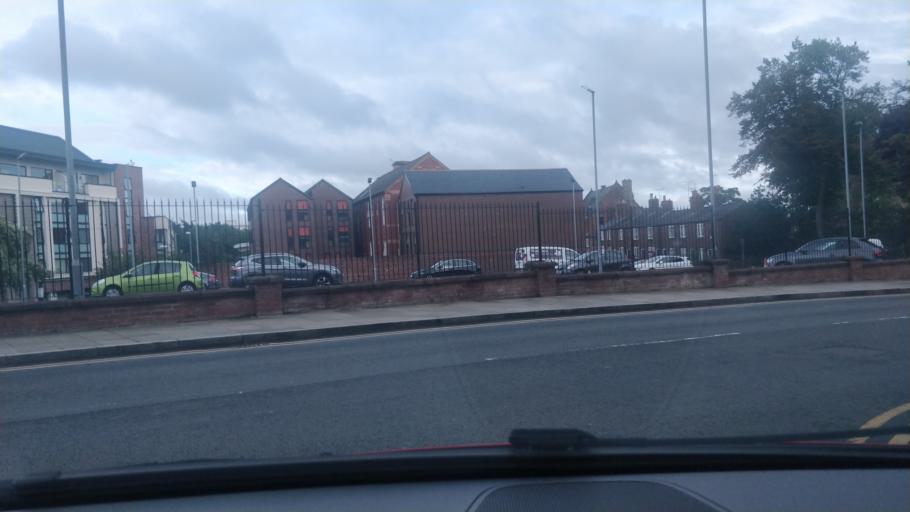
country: GB
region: England
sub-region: Cheshire West and Chester
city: Chester
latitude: 53.1949
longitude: -2.8916
